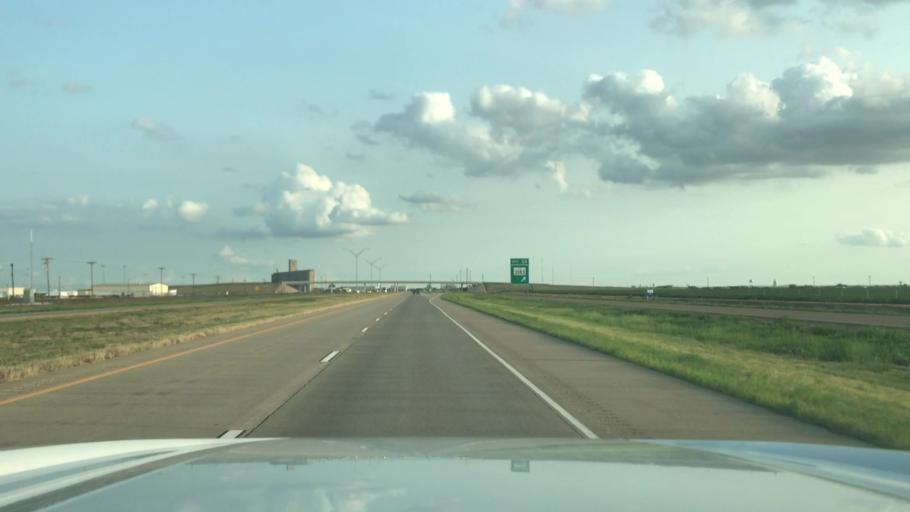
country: US
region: Texas
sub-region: Hale County
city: Seth Ward
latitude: 34.2548
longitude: -101.7091
